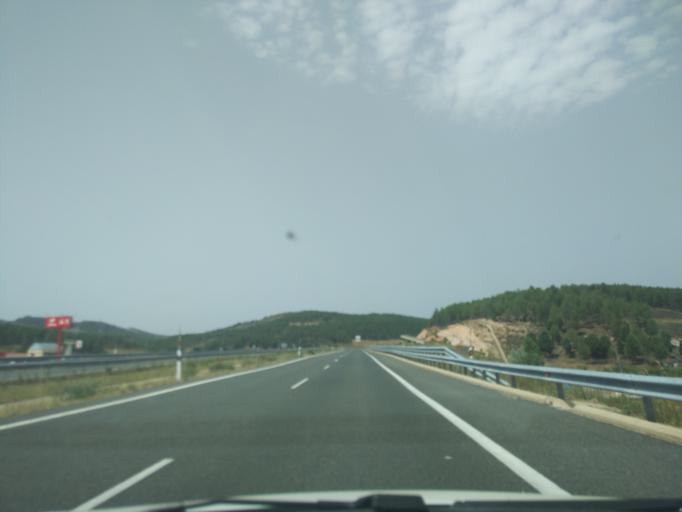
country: ES
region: Castille and Leon
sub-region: Provincia de Palencia
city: Alar del Rey
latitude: 42.7169
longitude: -4.2895
